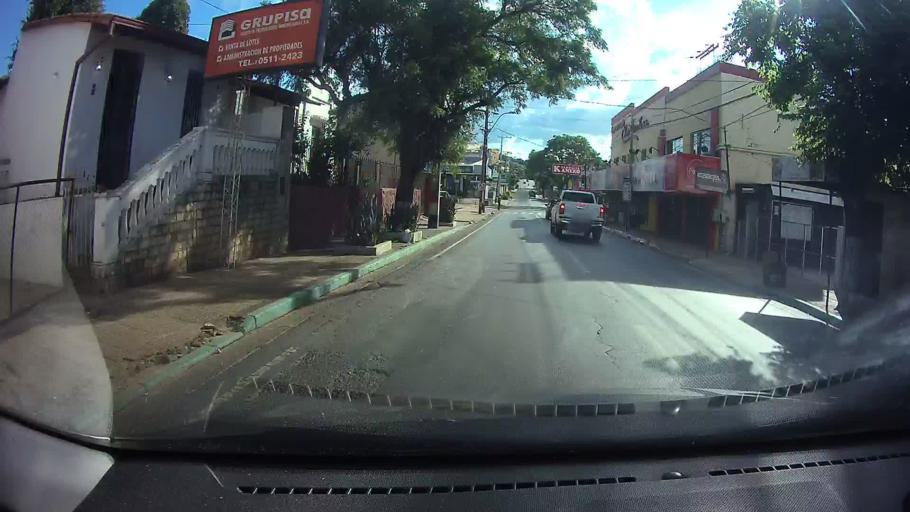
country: PY
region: Cordillera
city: Caacupe
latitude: -25.3864
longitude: -57.1439
